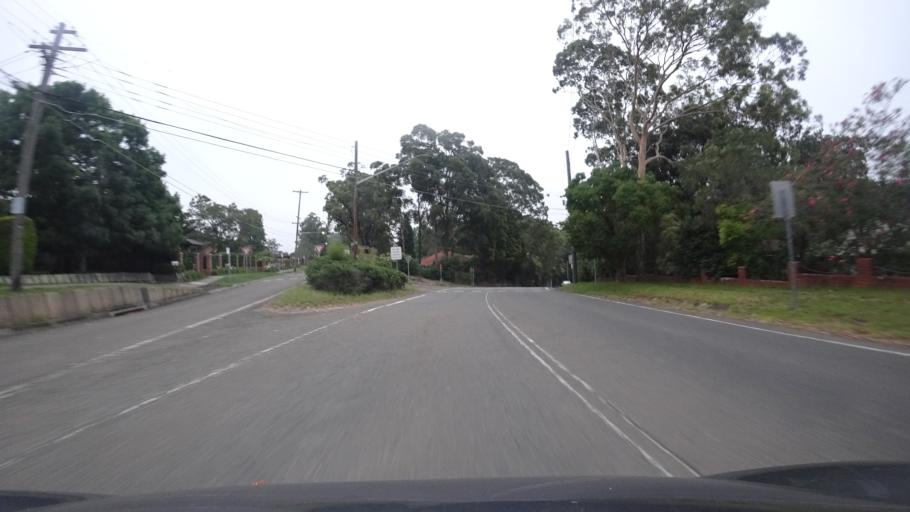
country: AU
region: New South Wales
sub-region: Ku-ring-gai
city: Normanhurst
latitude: -33.7355
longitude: 151.0970
